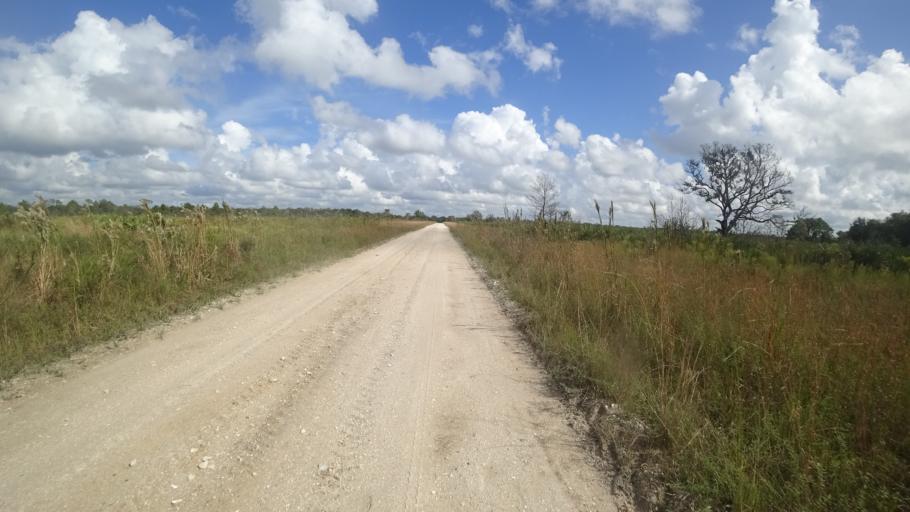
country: US
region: Florida
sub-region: Hillsborough County
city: Wimauma
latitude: 27.5175
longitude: -82.1307
